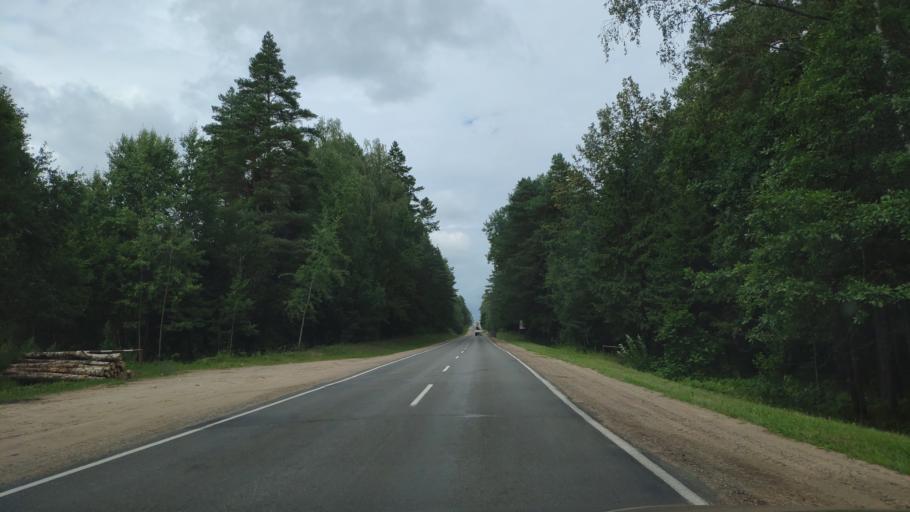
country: BY
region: Minsk
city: Novosel'ye
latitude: 53.9362
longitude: 27.2440
